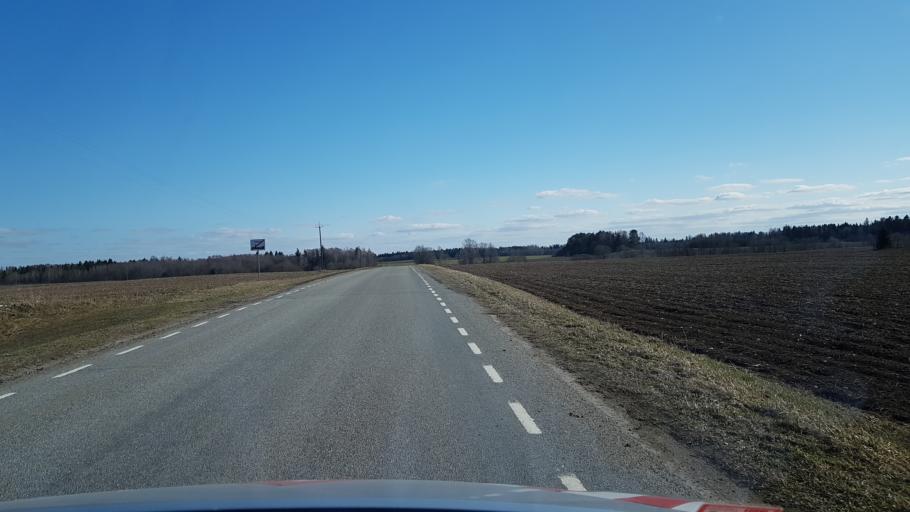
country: EE
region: Laeaene-Virumaa
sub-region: Kadrina vald
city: Kadrina
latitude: 59.3719
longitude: 26.0456
